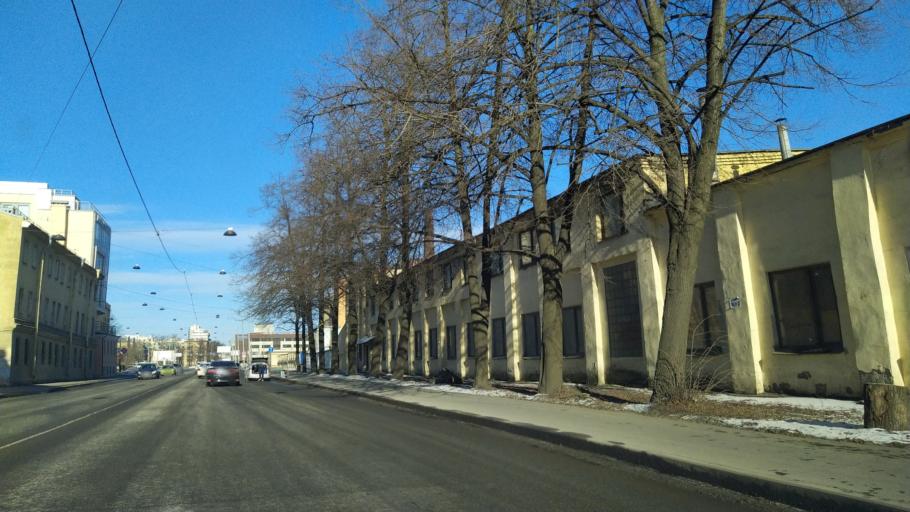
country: RU
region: St.-Petersburg
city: Centralniy
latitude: 59.9112
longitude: 30.3581
